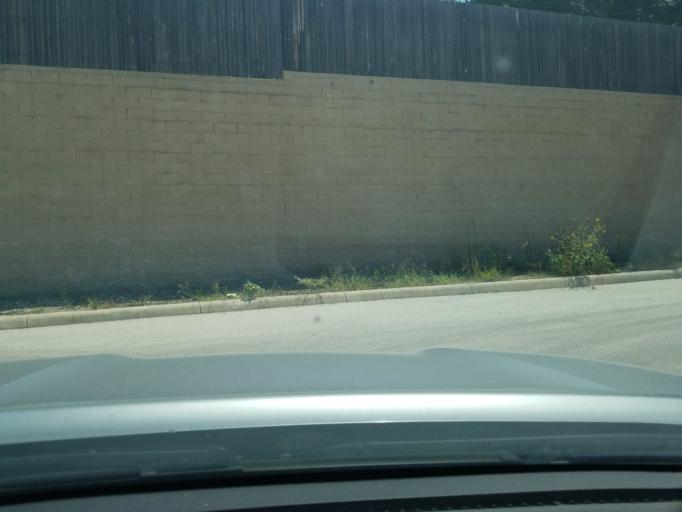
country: US
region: Texas
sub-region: Bexar County
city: Timberwood Park
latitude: 29.7074
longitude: -98.4819
